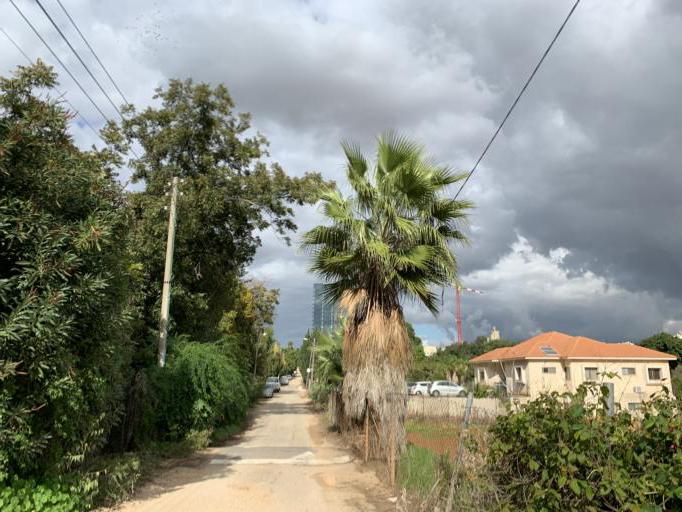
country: IL
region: Central District
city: Hod HaSharon
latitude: 32.1689
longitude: 34.8913
